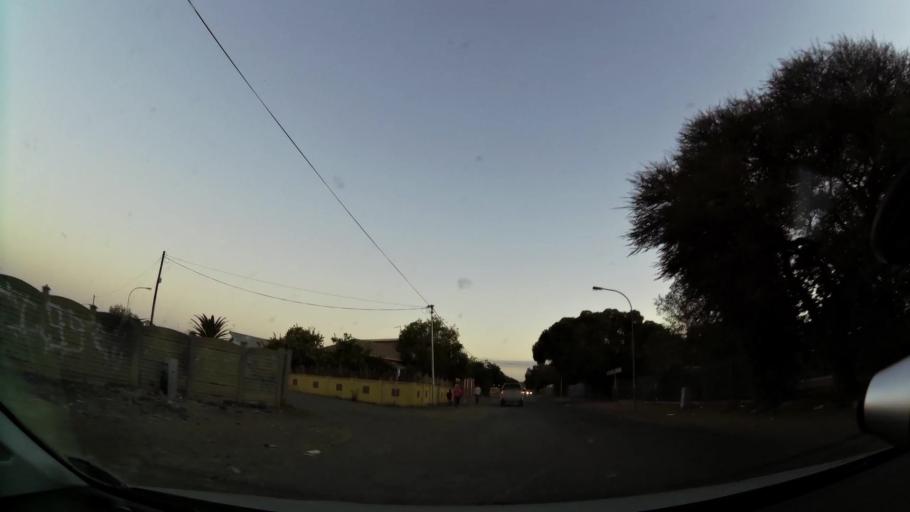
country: ZA
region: Northern Cape
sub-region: Frances Baard District Municipality
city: Kimberley
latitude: -28.7241
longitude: 24.7669
